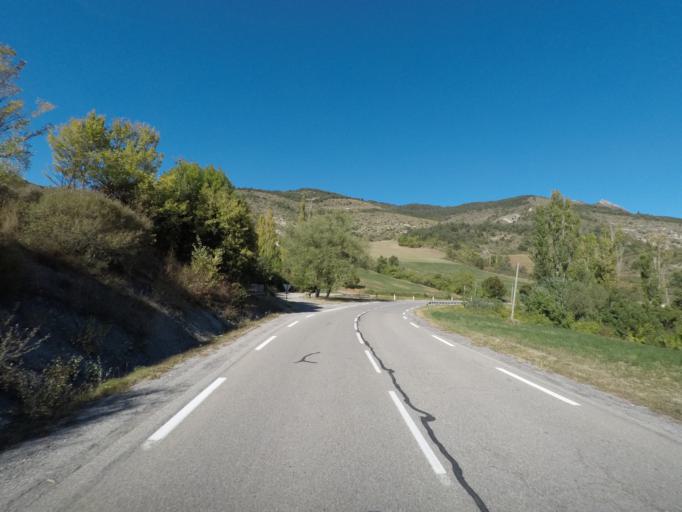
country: FR
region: Provence-Alpes-Cote d'Azur
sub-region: Departement des Hautes-Alpes
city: Serres
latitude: 44.4049
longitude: 5.5080
